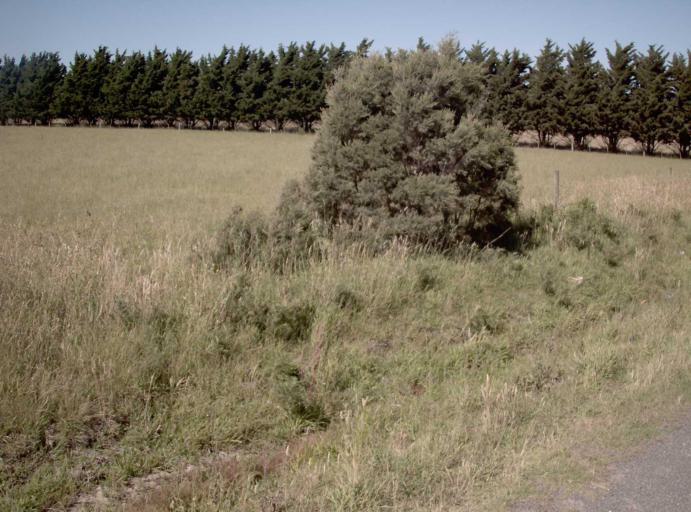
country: AU
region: Victoria
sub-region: Latrobe
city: Morwell
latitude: -38.6648
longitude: 146.4266
